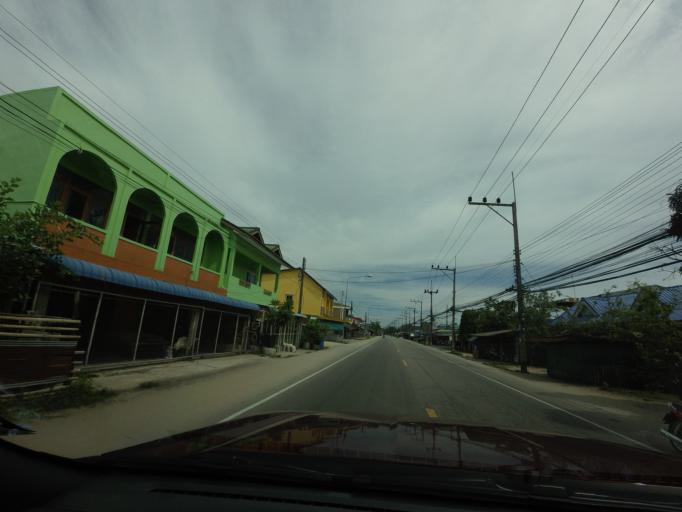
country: TH
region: Narathiwat
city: Tak Bai
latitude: 6.2545
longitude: 102.0606
